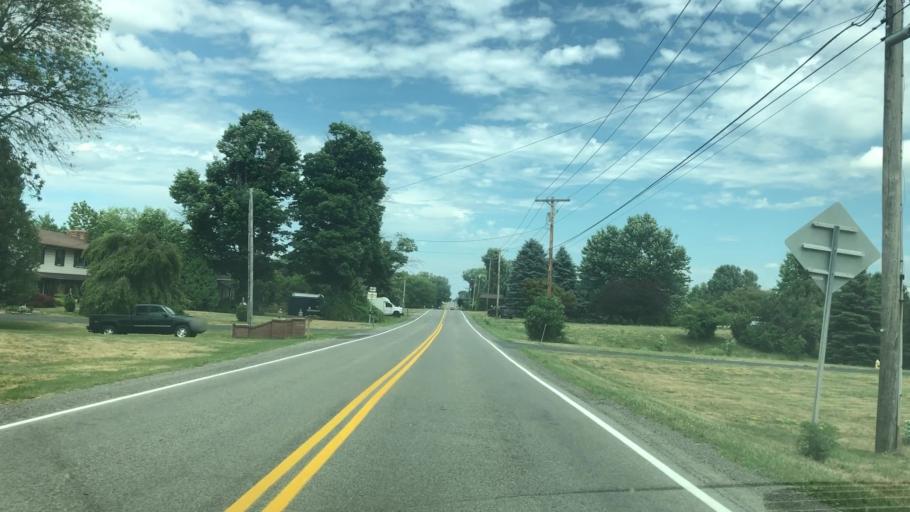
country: US
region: New York
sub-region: Monroe County
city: Webster
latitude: 43.1612
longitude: -77.4005
